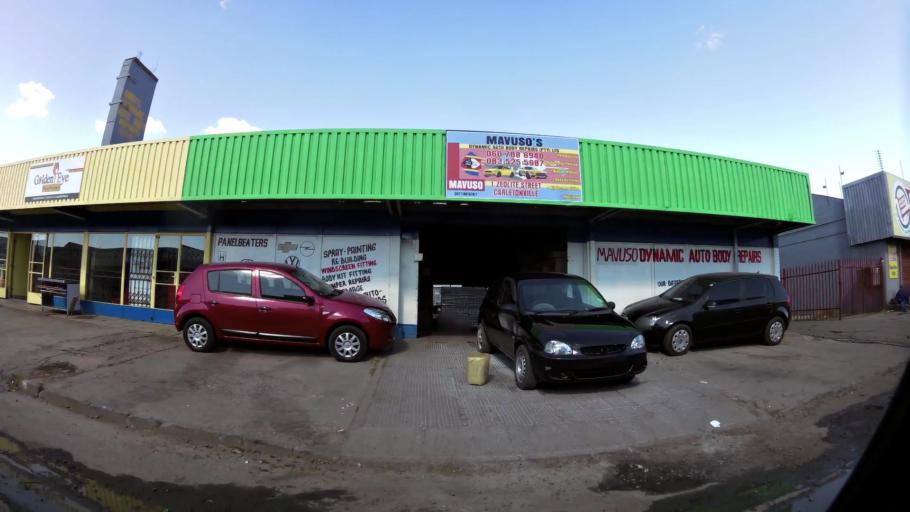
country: ZA
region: Gauteng
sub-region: West Rand District Municipality
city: Carletonville
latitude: -26.3543
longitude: 27.3956
